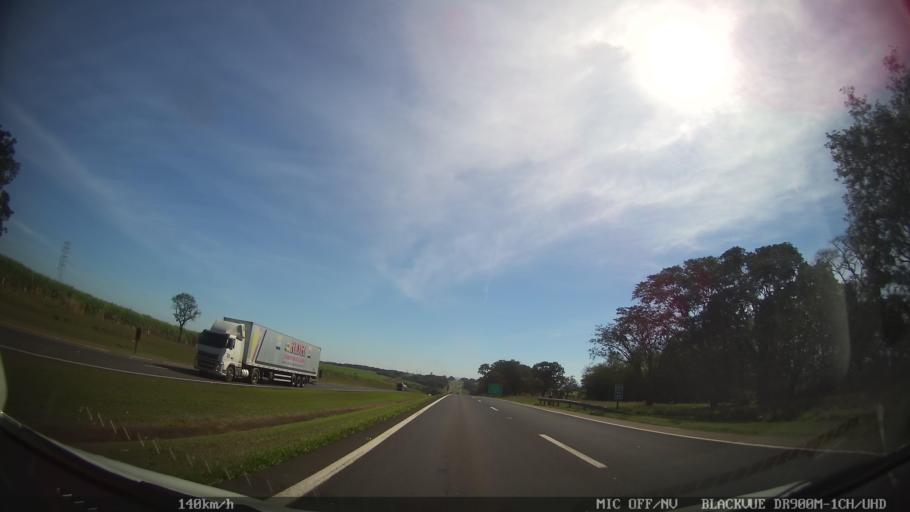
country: BR
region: Sao Paulo
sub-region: Porto Ferreira
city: Porto Ferreira
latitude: -21.9233
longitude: -47.4712
